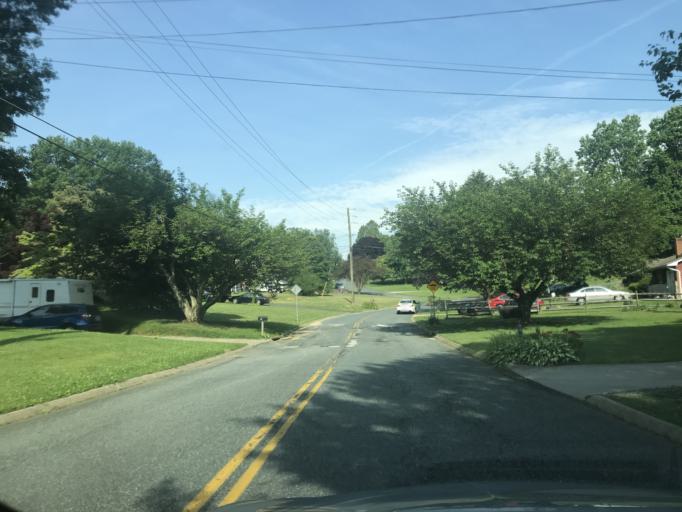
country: US
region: Maryland
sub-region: Harford County
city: Bel Air North
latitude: 39.5569
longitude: -76.3924
